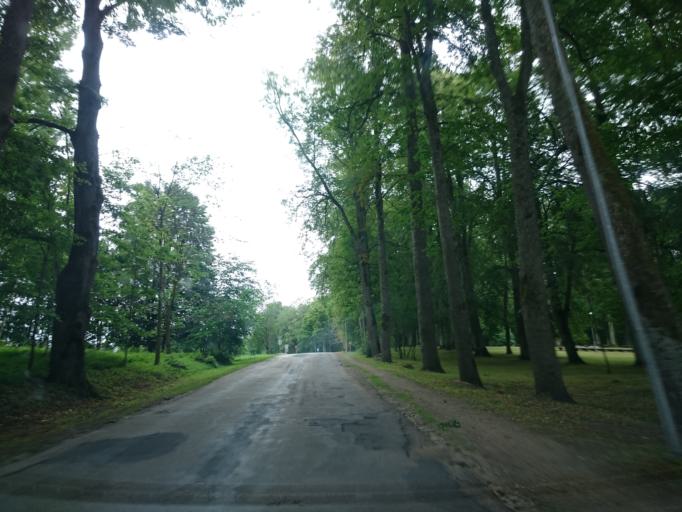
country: LV
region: Pavilostas
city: Pavilosta
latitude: 56.8802
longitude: 21.2108
